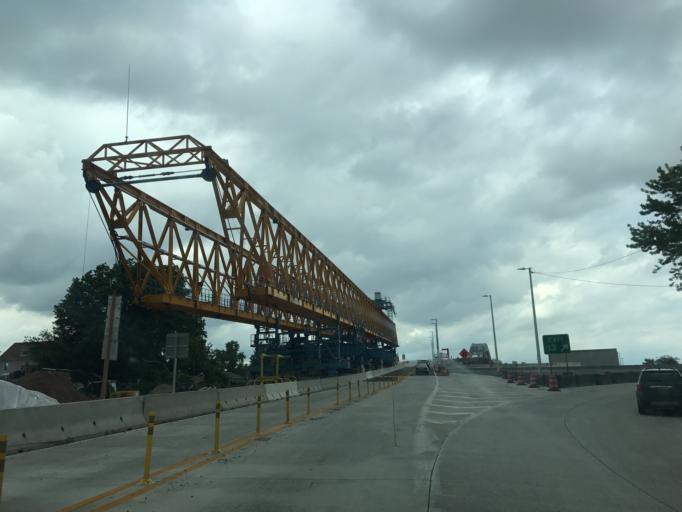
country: US
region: New York
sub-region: Richmond County
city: Bloomfield
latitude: 40.6314
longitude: -74.1456
